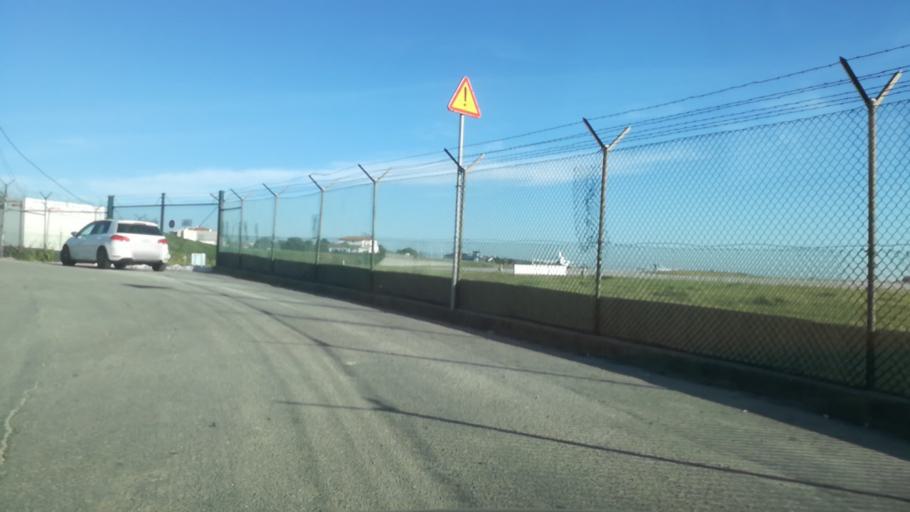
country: PT
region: Porto
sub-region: Matosinhos
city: Santa Cruz do Bispo
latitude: 41.2490
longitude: -8.6793
